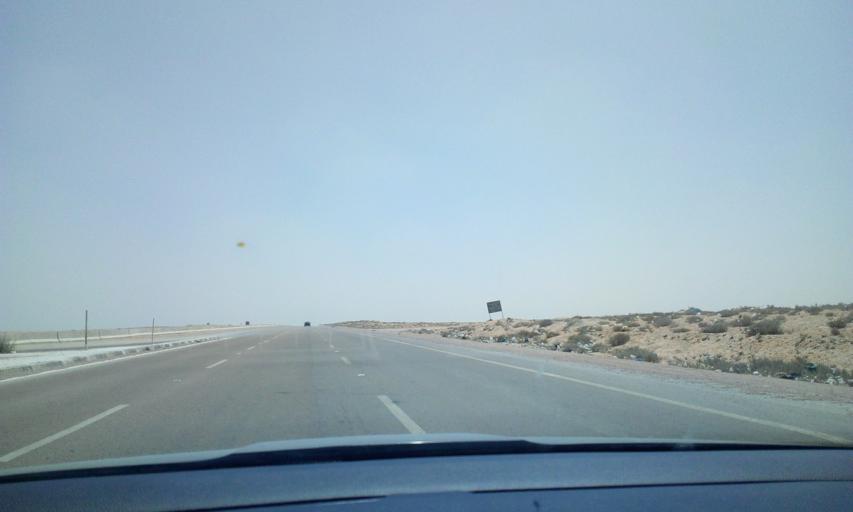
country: EG
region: Al Buhayrah
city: Abu al Matamir
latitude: 30.6100
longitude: 29.8248
